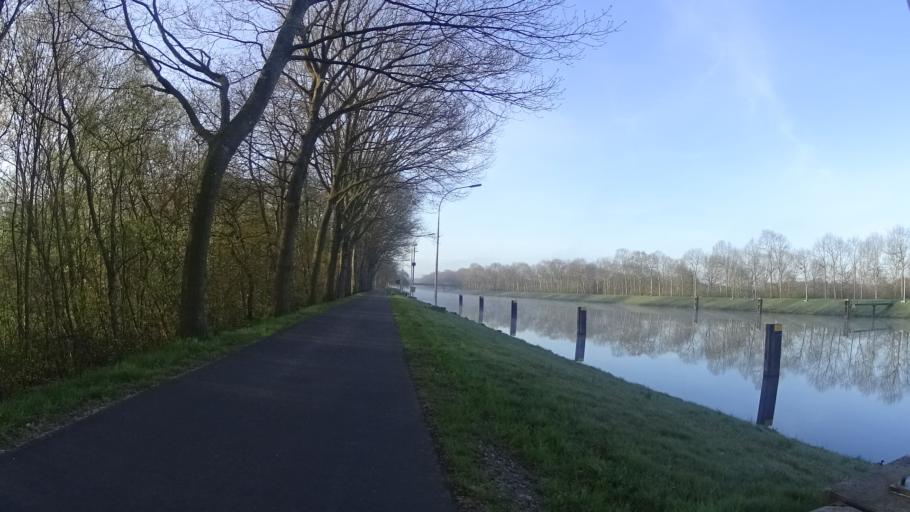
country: DE
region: Lower Saxony
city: Fresenburg
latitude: 52.9004
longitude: 7.3125
